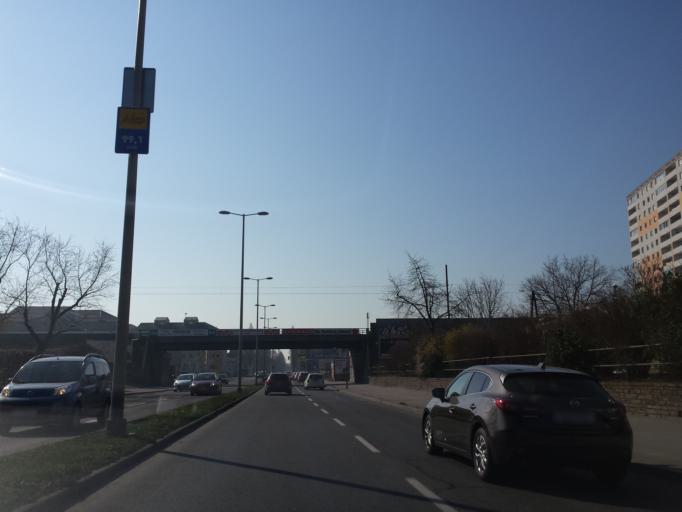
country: AT
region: Styria
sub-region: Graz Stadt
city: Graz
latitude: 47.0565
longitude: 15.4270
